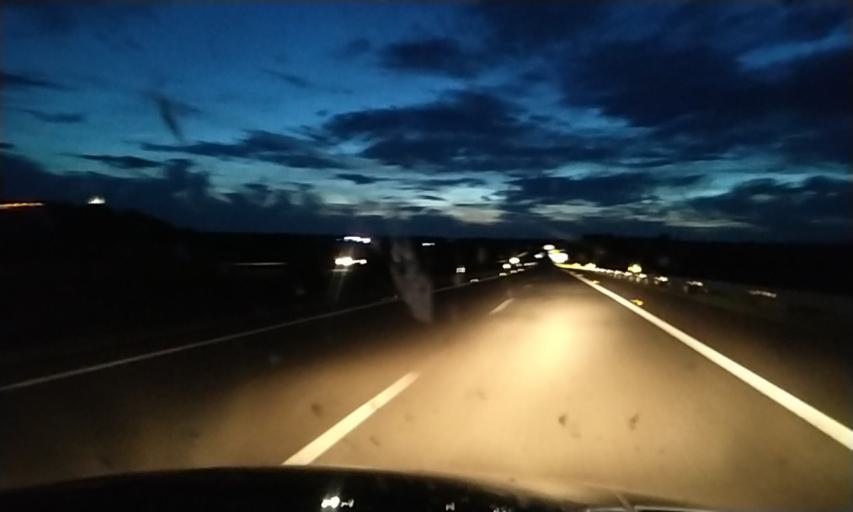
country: ES
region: Extremadura
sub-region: Provincia de Caceres
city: Galisteo
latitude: 39.9828
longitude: -6.2529
